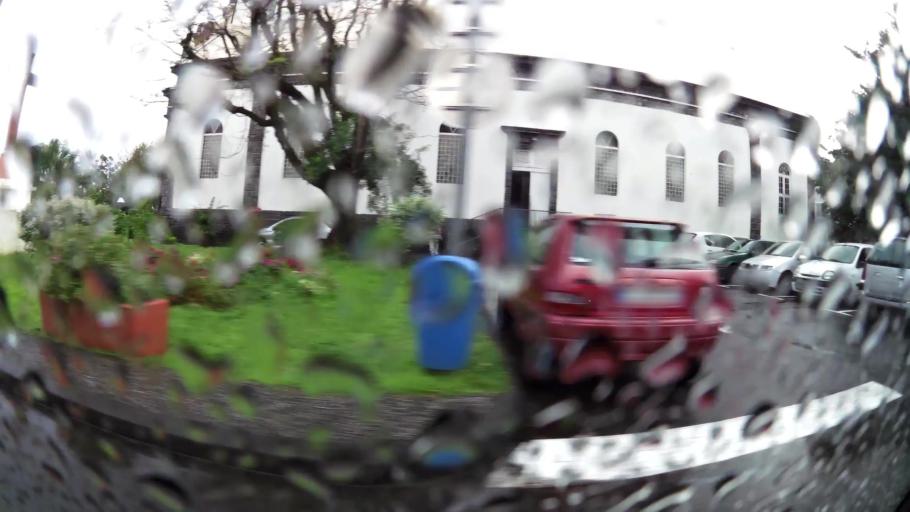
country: RE
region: Reunion
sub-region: Reunion
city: Saint-Benoit
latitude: -21.0337
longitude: 55.7121
